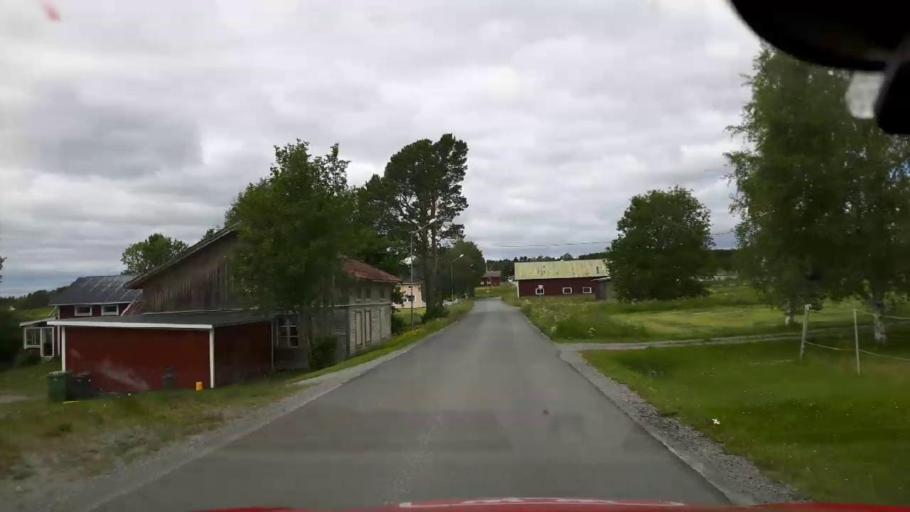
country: SE
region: Jaemtland
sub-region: OEstersunds Kommun
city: Brunflo
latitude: 63.0784
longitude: 14.8760
